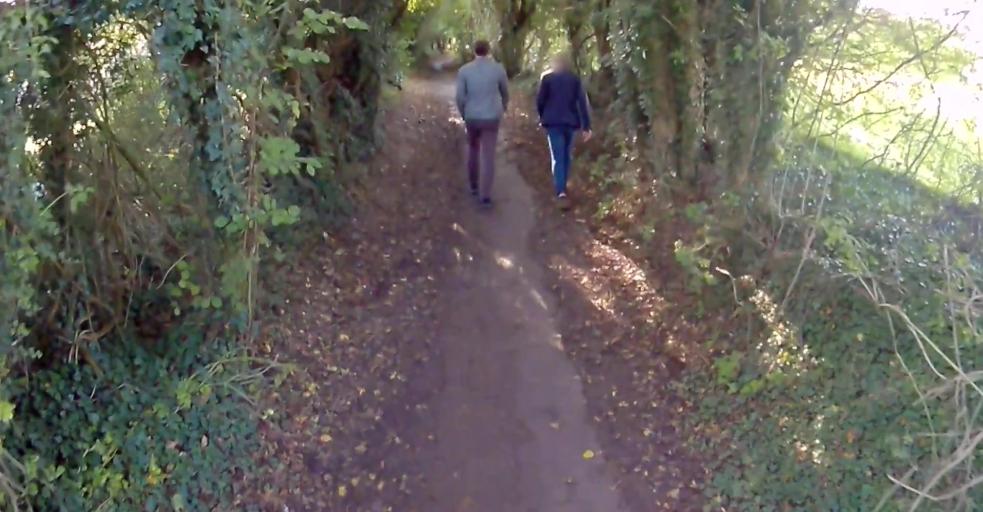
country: GB
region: England
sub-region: Hampshire
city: Odiham
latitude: 51.2454
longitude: -0.9410
